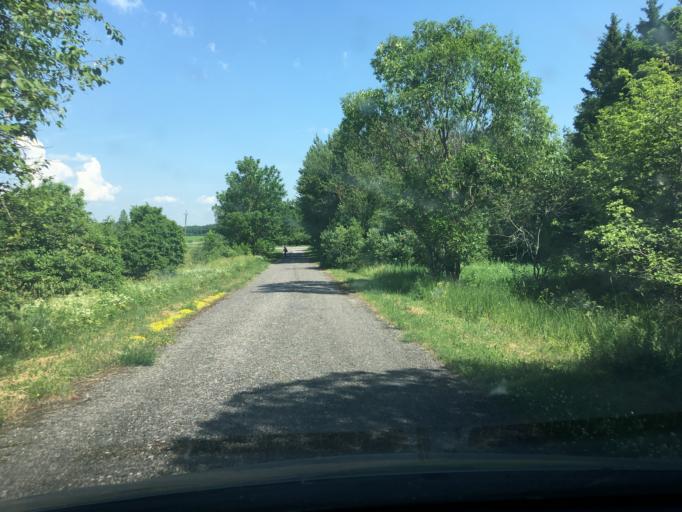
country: EE
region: Laeaene
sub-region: Lihula vald
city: Lihula
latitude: 58.6675
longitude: 23.7646
